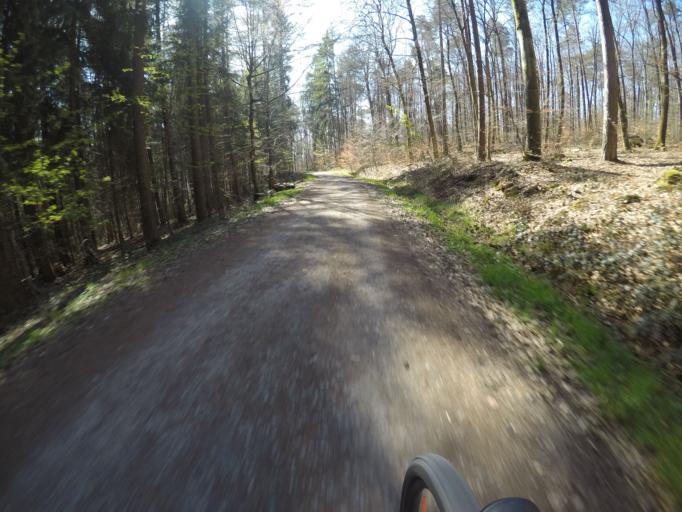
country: DE
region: Baden-Wuerttemberg
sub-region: Regierungsbezirk Stuttgart
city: Filderstadt
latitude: 48.6321
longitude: 9.2140
